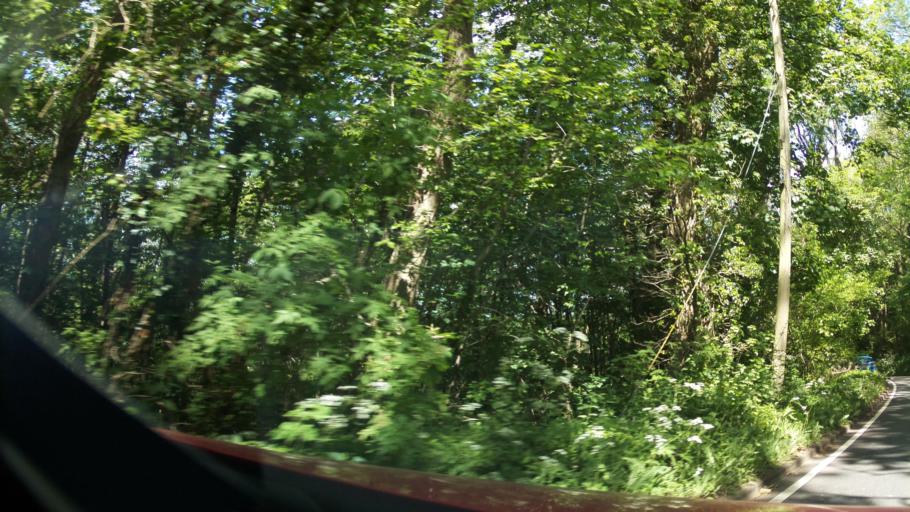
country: GB
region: Wales
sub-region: Monmouthshire
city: Mitchel Troy
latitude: 51.7726
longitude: -2.7323
